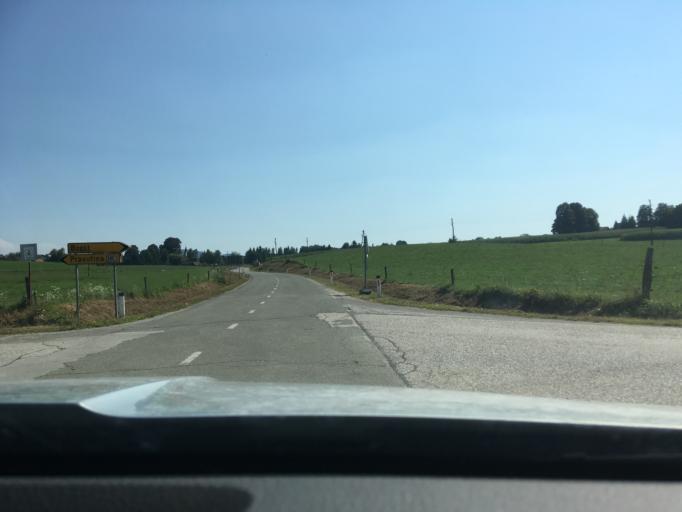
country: SI
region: Metlika
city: Metlika
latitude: 45.5953
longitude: 15.2772
